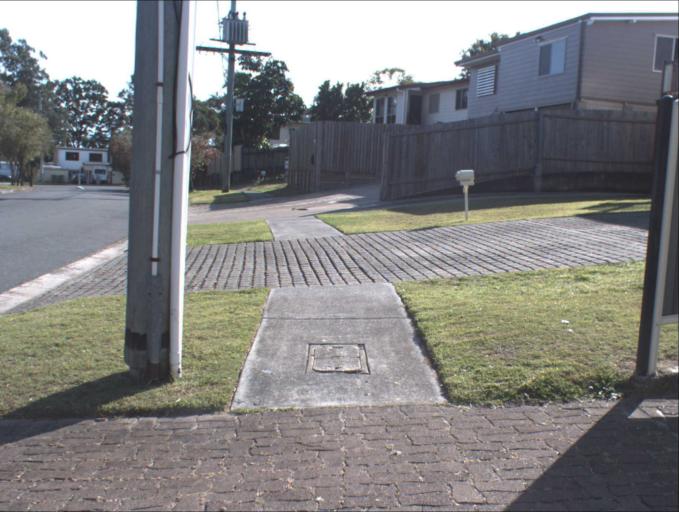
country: AU
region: Queensland
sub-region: Logan
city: Waterford West
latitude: -27.6834
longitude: 153.0971
